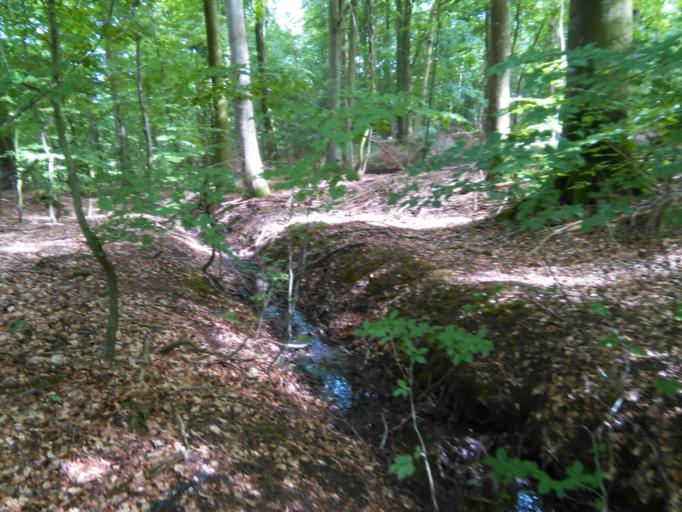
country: DK
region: Central Jutland
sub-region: Arhus Kommune
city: Beder
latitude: 56.0603
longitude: 10.2516
